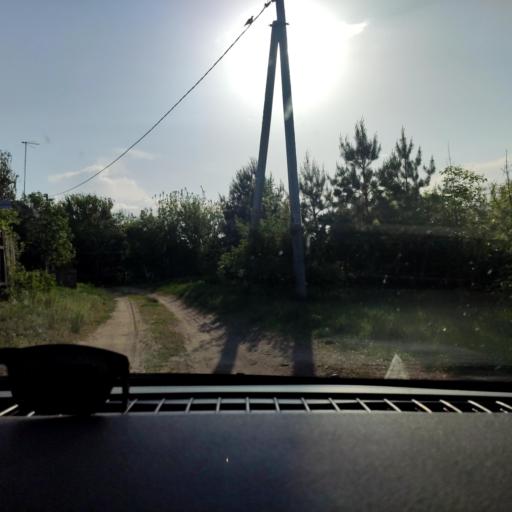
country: RU
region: Samara
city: Volzhskiy
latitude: 53.4386
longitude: 50.1700
